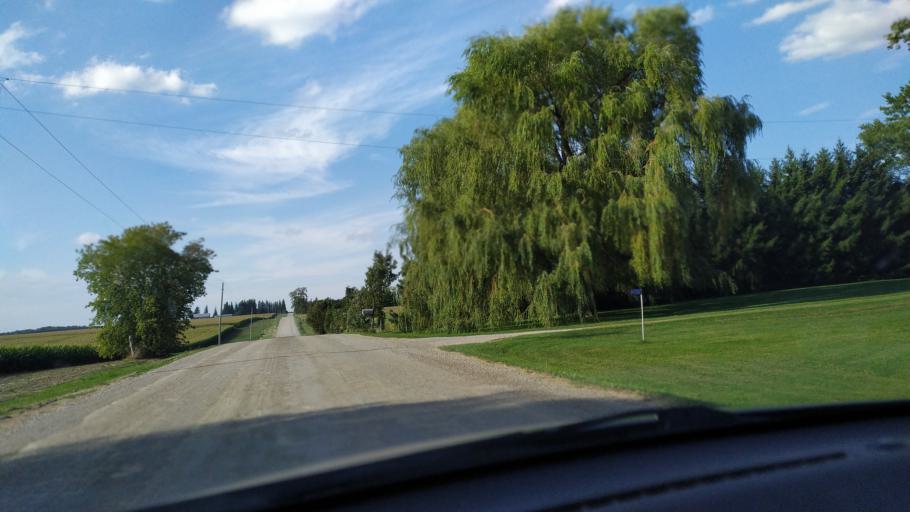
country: CA
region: Ontario
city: Stratford
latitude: 43.2722
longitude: -80.9407
